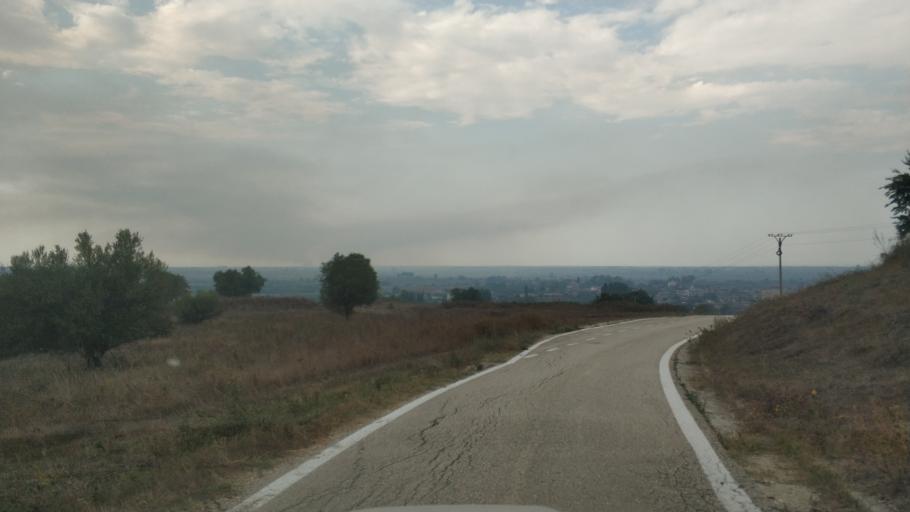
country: AL
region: Fier
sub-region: Rrethi i Fierit
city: Dermenas
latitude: 40.7231
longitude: 19.4692
